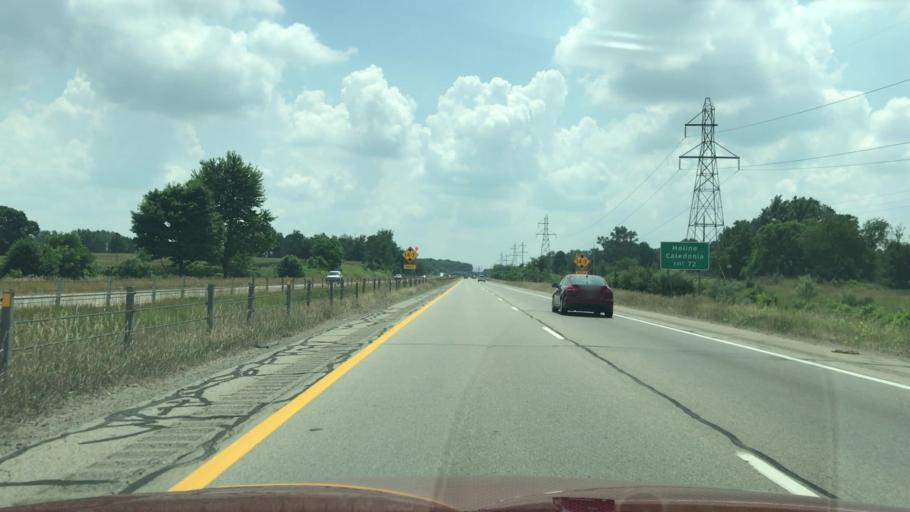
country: US
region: Michigan
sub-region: Kent County
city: Cutlerville
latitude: 42.7924
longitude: -85.6686
